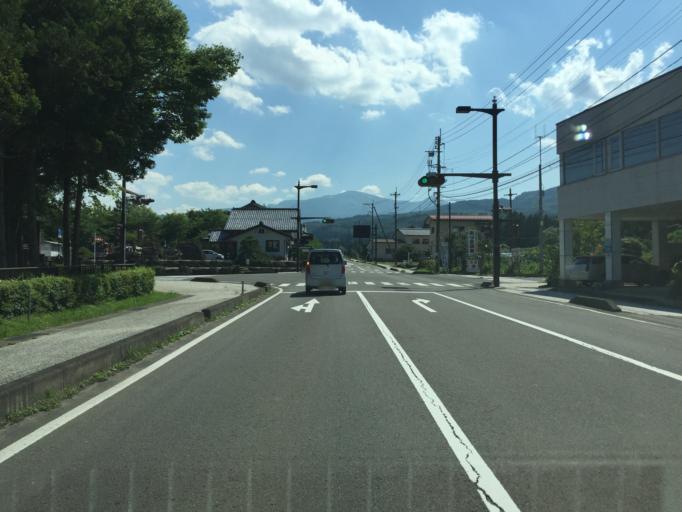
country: JP
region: Fukushima
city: Fukushima-shi
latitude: 37.7214
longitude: 140.3576
